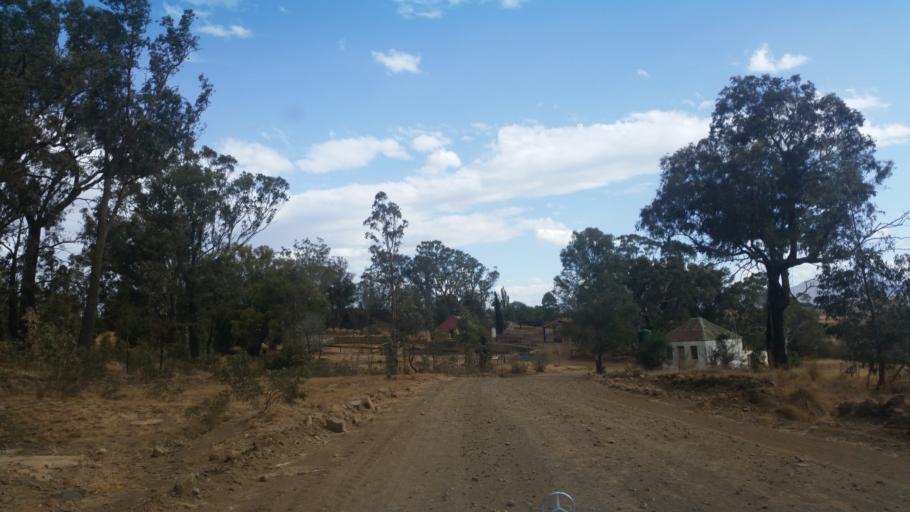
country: ZA
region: Orange Free State
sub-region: Thabo Mofutsanyana District Municipality
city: Phuthaditjhaba
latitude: -28.3460
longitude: 28.6145
